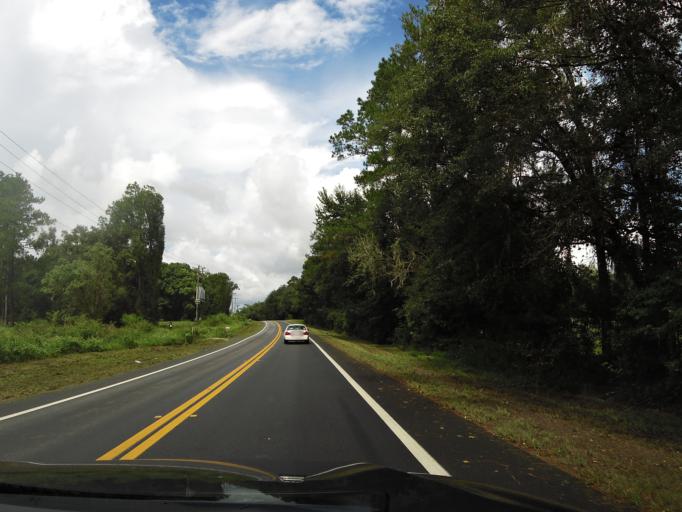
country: US
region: Florida
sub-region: Clay County
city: Middleburg
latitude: 30.1317
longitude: -81.9993
